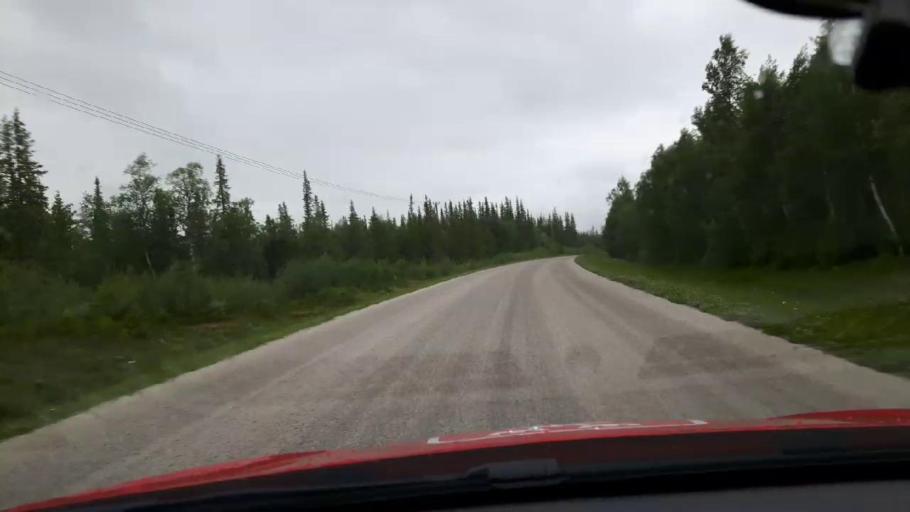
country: NO
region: Nord-Trondelag
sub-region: Meraker
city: Meraker
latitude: 63.2708
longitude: 12.3695
